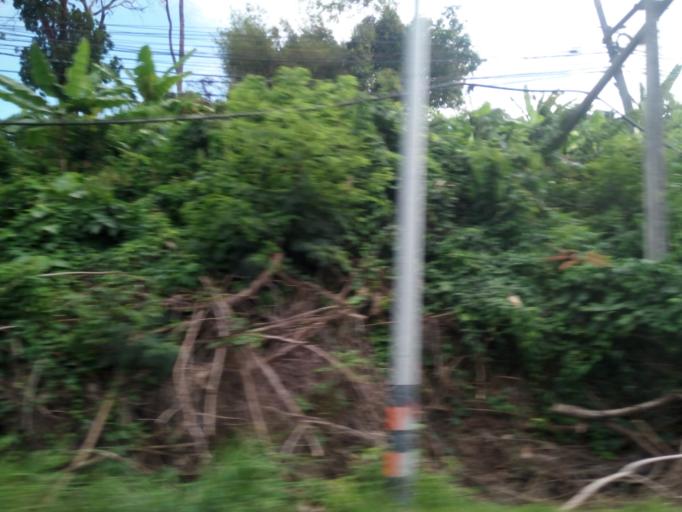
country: TH
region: Phuket
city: Mueang Phuket
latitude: 7.8427
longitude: 98.3894
